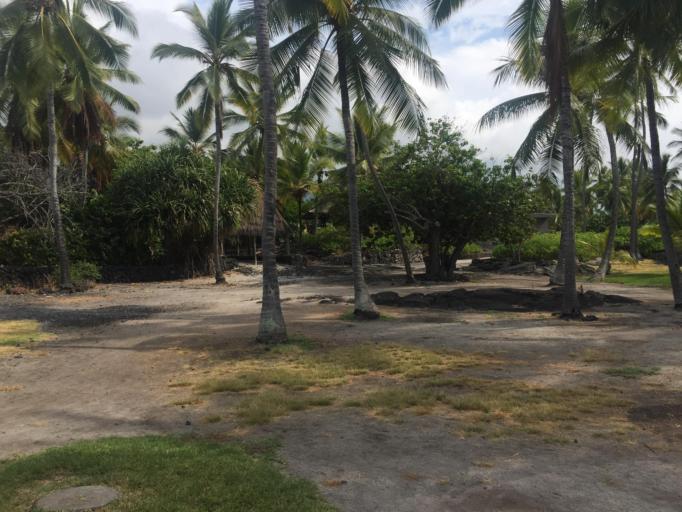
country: US
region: Hawaii
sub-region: Hawaii County
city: Honaunau-Napoopoo
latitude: 19.4222
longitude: -155.9111
